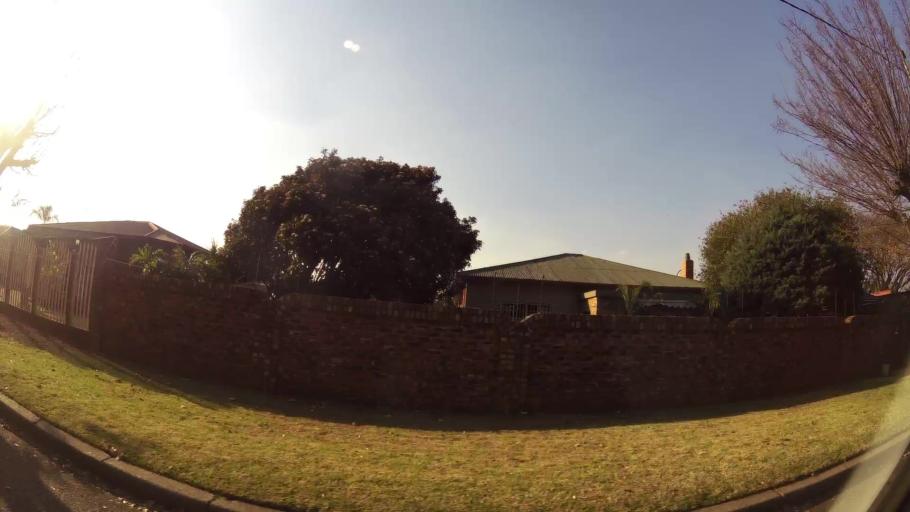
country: ZA
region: Gauteng
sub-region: Ekurhuleni Metropolitan Municipality
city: Brakpan
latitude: -26.2540
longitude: 28.3721
